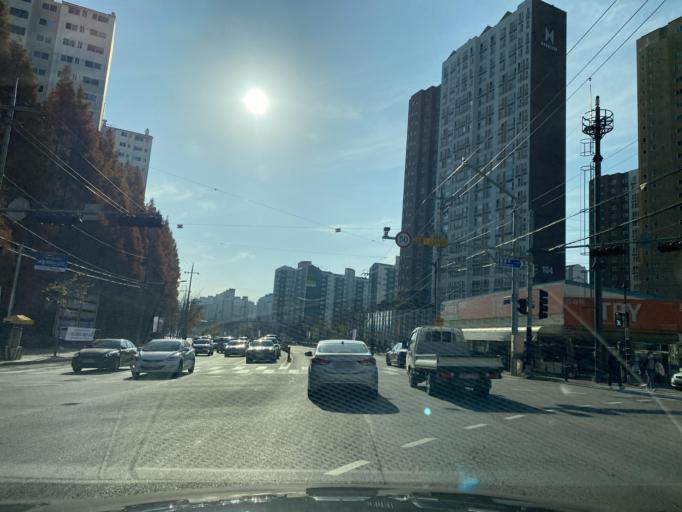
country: KR
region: Chungcheongnam-do
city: Cheonan
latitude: 36.7925
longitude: 127.1215
